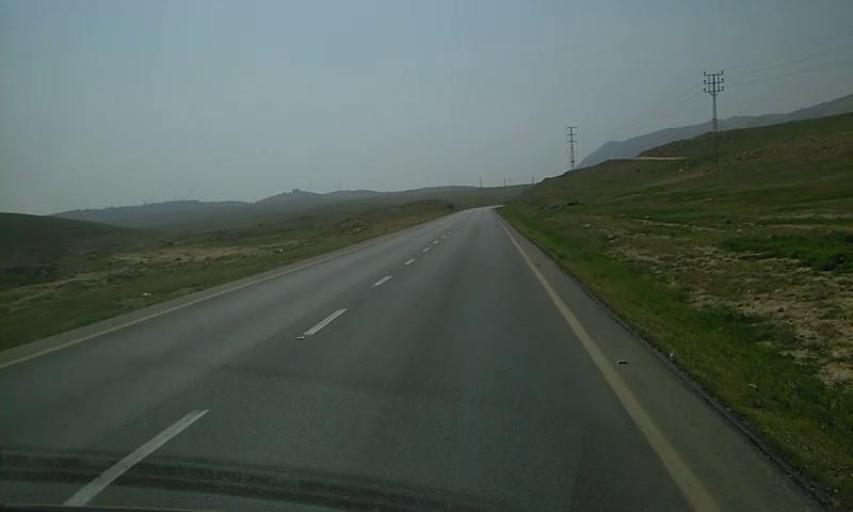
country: PS
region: West Bank
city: An Nuway`imah
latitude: 31.9158
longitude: 35.4205
